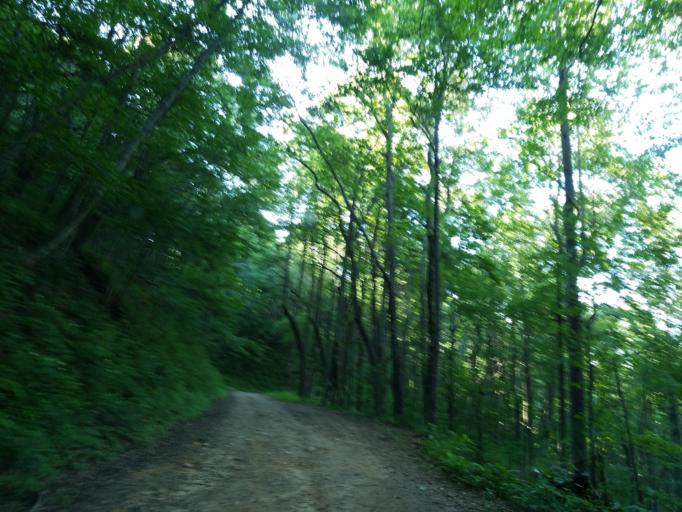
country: US
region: Georgia
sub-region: Dawson County
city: Dawsonville
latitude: 34.6057
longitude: -84.2138
